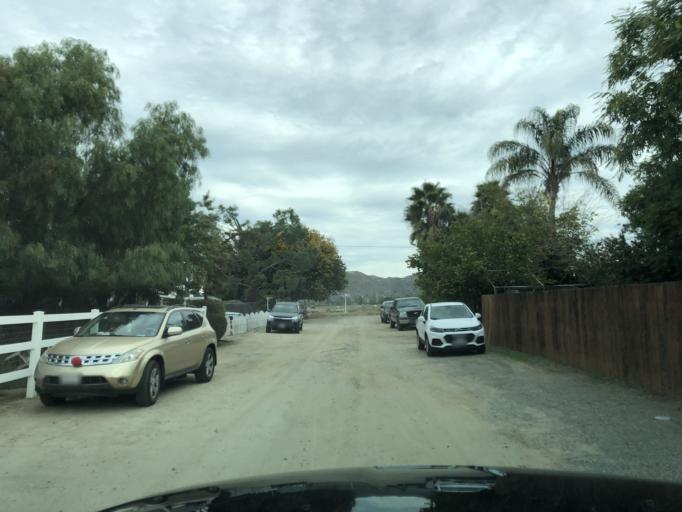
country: US
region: California
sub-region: Riverside County
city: Wildomar
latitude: 33.6225
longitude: -117.2745
